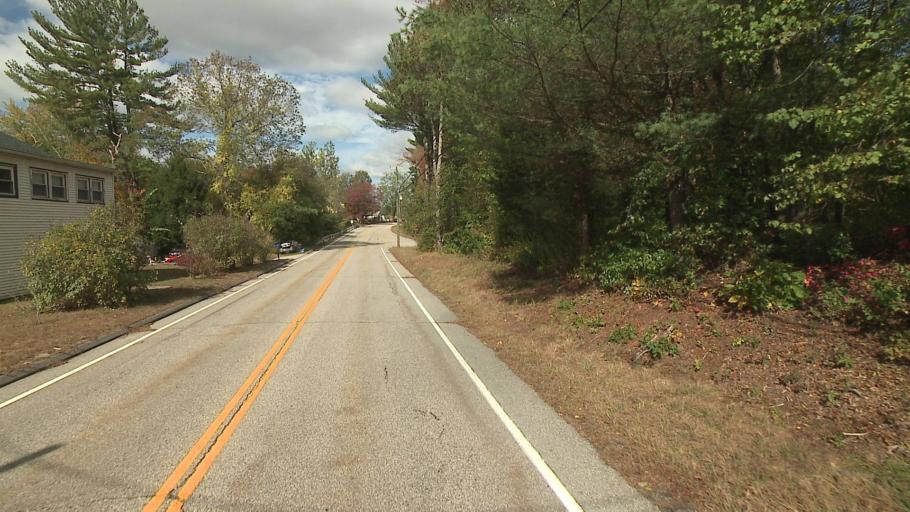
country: US
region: Connecticut
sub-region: Windham County
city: Putnam
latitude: 41.8978
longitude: -71.8857
